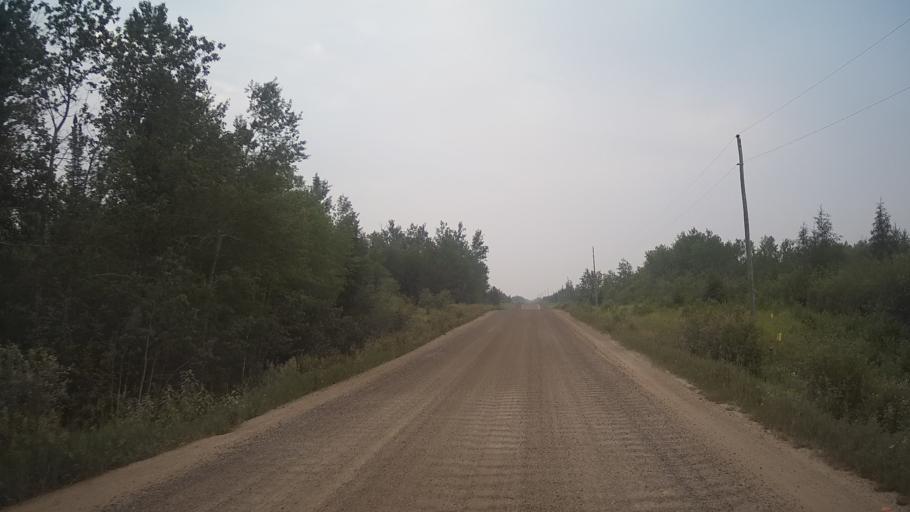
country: CA
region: Ontario
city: Hearst
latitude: 49.6352
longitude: -83.2783
